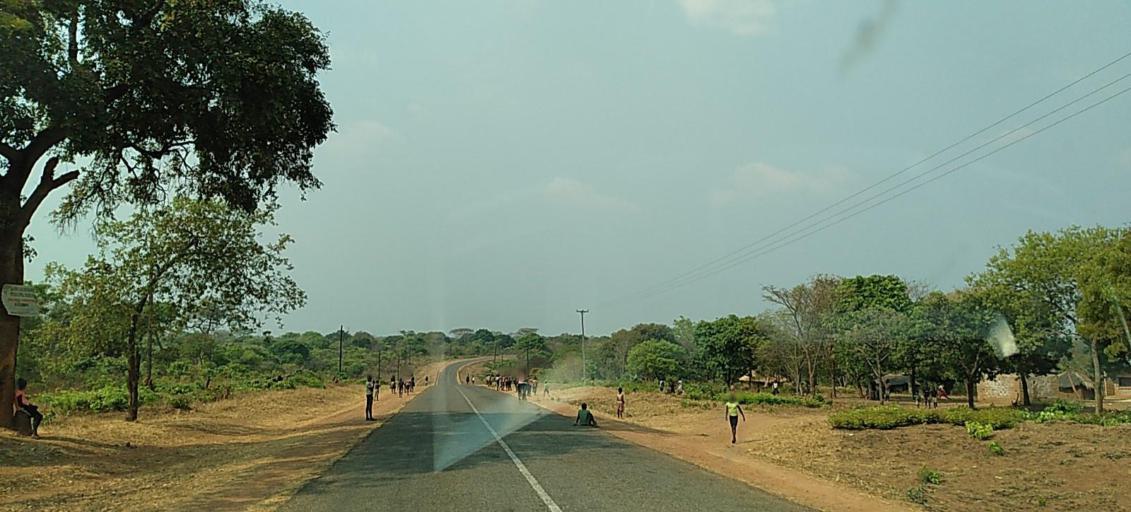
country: ZM
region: North-Western
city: Kabompo
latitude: -13.5394
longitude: 24.2719
